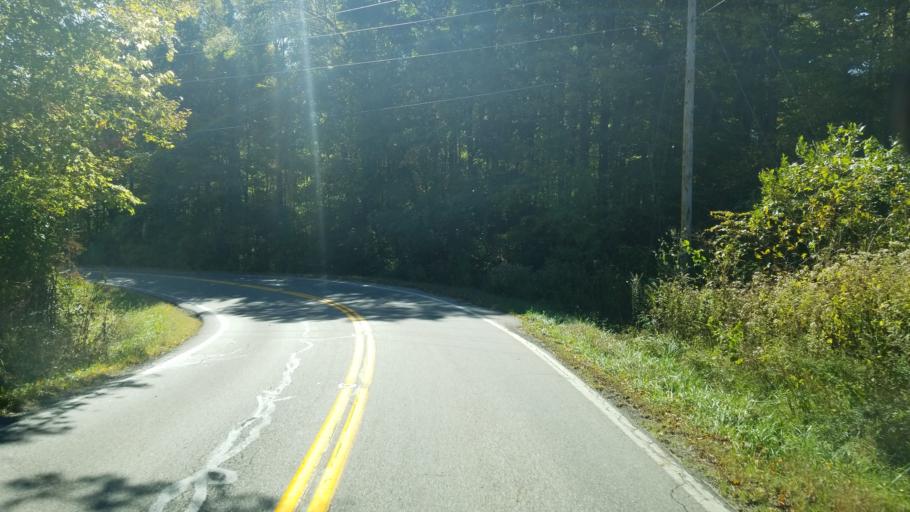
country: US
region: Ohio
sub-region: Highland County
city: Leesburg
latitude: 39.2732
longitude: -83.4831
